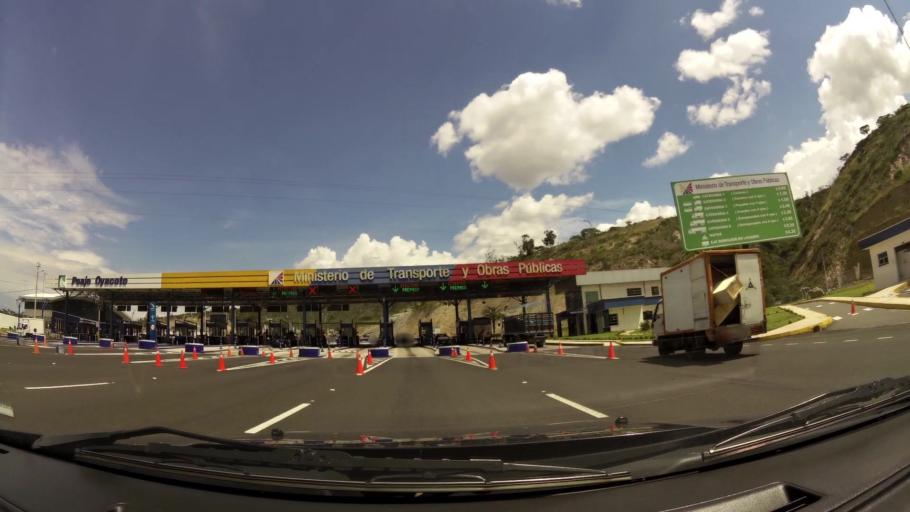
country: EC
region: Pichincha
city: Quito
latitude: -0.0988
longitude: -78.4070
